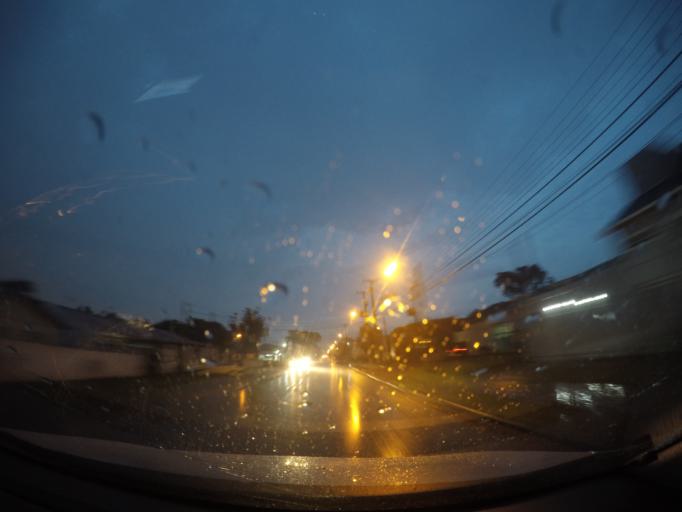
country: BR
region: Parana
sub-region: Sao Jose Dos Pinhais
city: Sao Jose dos Pinhais
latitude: -25.5022
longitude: -49.2332
